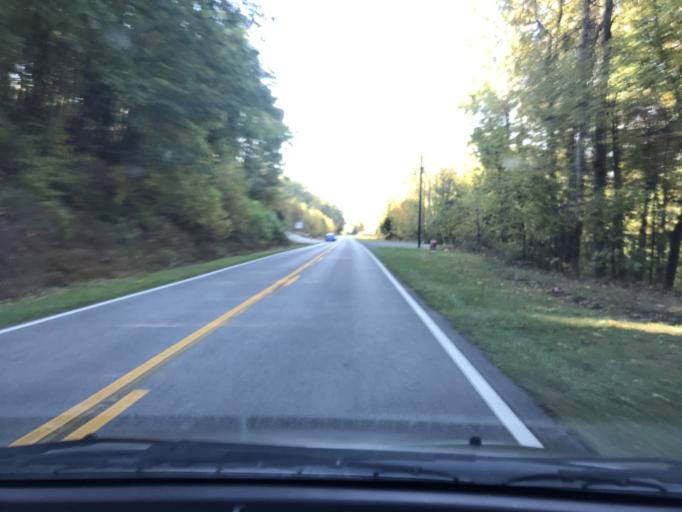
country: US
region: Georgia
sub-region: Dade County
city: Trenton
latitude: 34.8936
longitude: -85.4545
